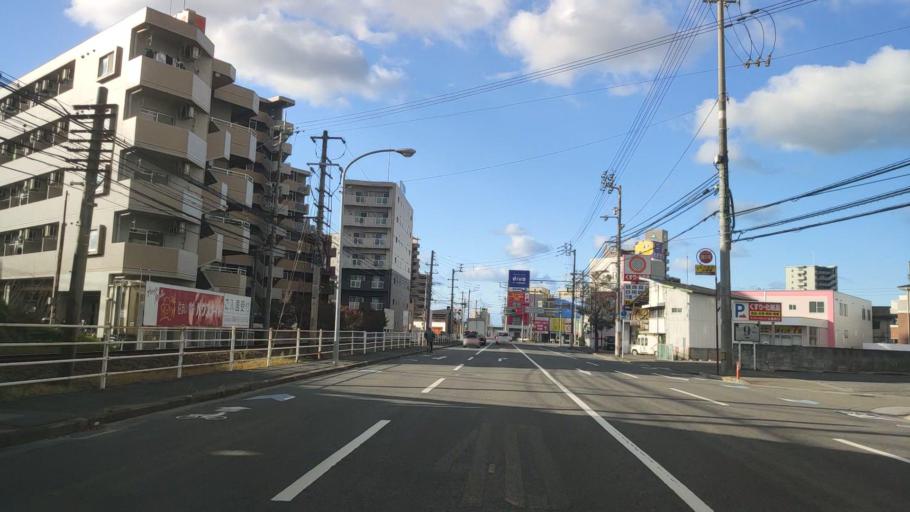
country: JP
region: Ehime
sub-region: Shikoku-chuo Shi
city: Matsuyama
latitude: 33.8295
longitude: 132.7516
